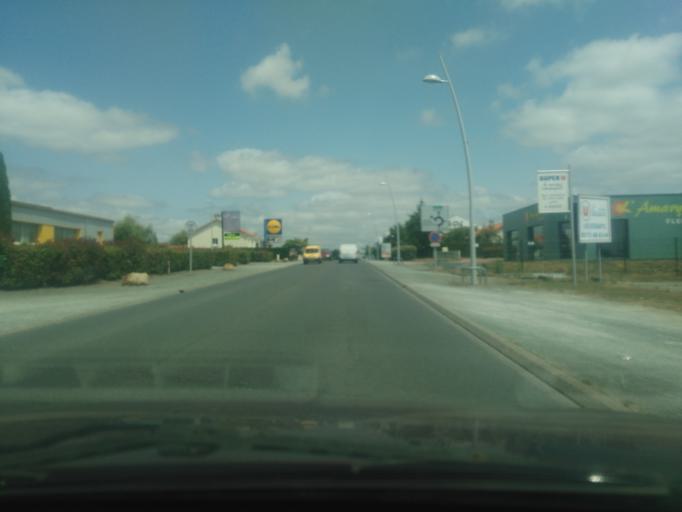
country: FR
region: Pays de la Loire
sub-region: Departement de la Vendee
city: Les Essarts
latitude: 46.7667
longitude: -1.2353
